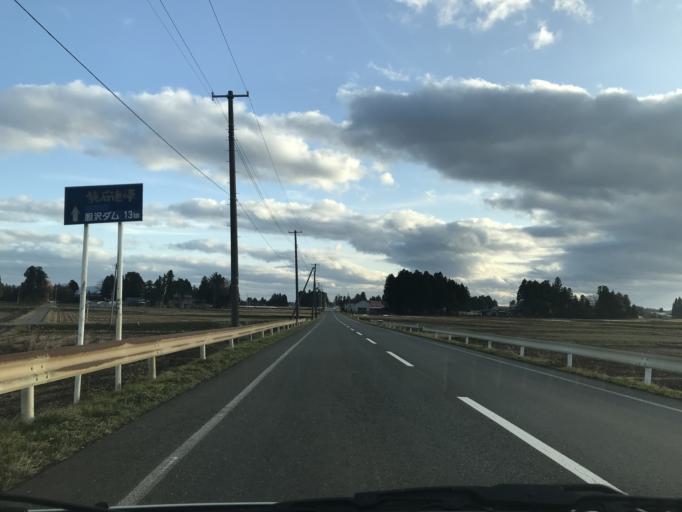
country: JP
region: Iwate
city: Mizusawa
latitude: 39.1466
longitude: 141.0484
